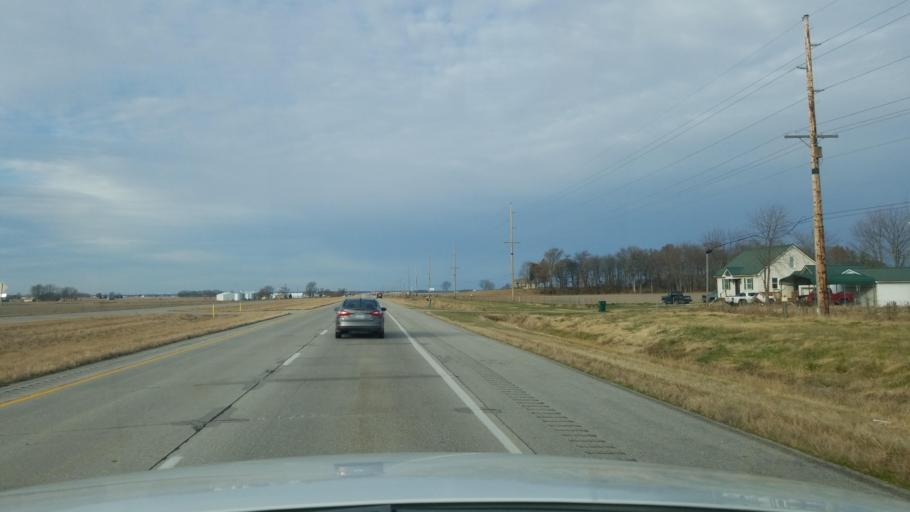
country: US
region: Indiana
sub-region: Posey County
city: Mount Vernon
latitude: 37.9422
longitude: -87.7587
